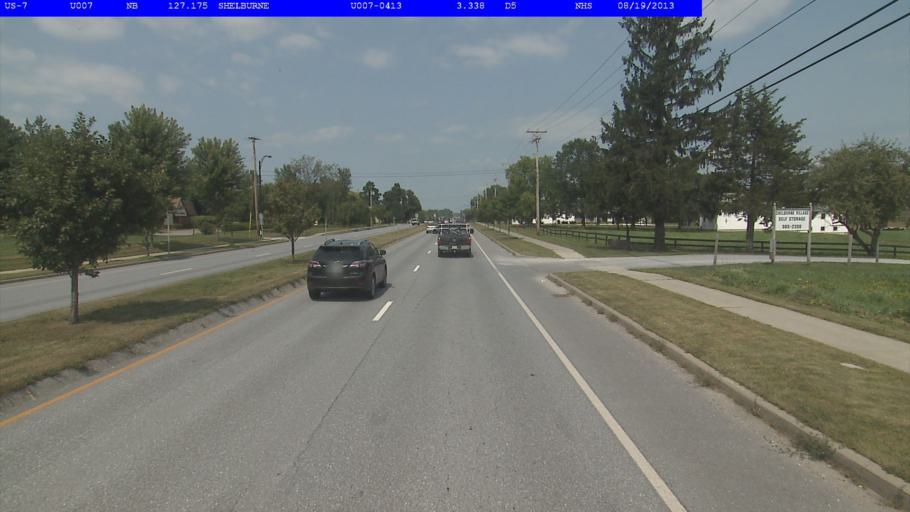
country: US
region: Vermont
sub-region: Chittenden County
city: Burlington
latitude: 44.3985
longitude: -73.2190
